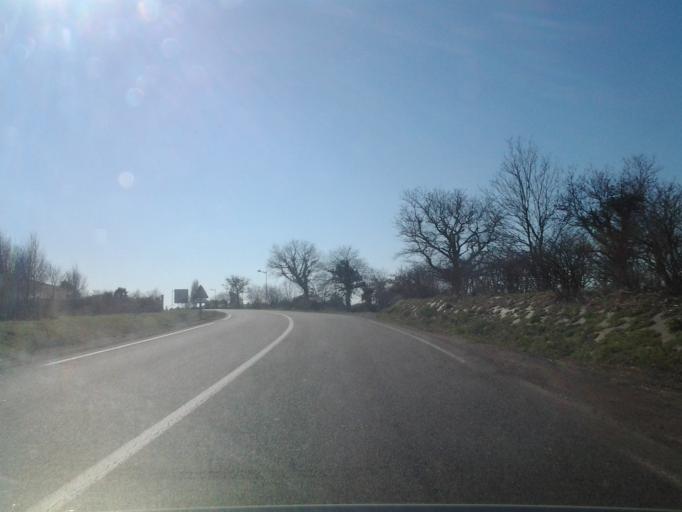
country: FR
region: Pays de la Loire
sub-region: Departement de la Vendee
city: Saint-Mathurin
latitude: 46.5722
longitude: -1.7070
